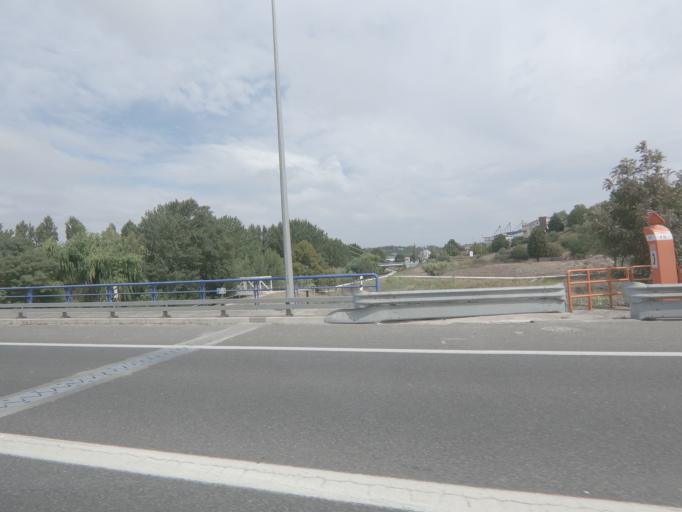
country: PT
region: Leiria
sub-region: Leiria
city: Leiria
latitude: 39.7514
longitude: -8.8173
